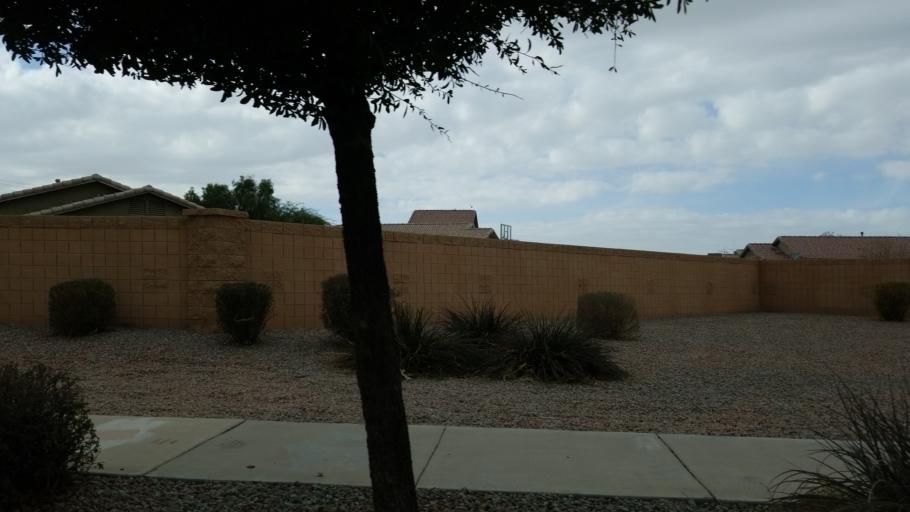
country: US
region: Arizona
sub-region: Maricopa County
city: Laveen
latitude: 33.4168
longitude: -112.1954
